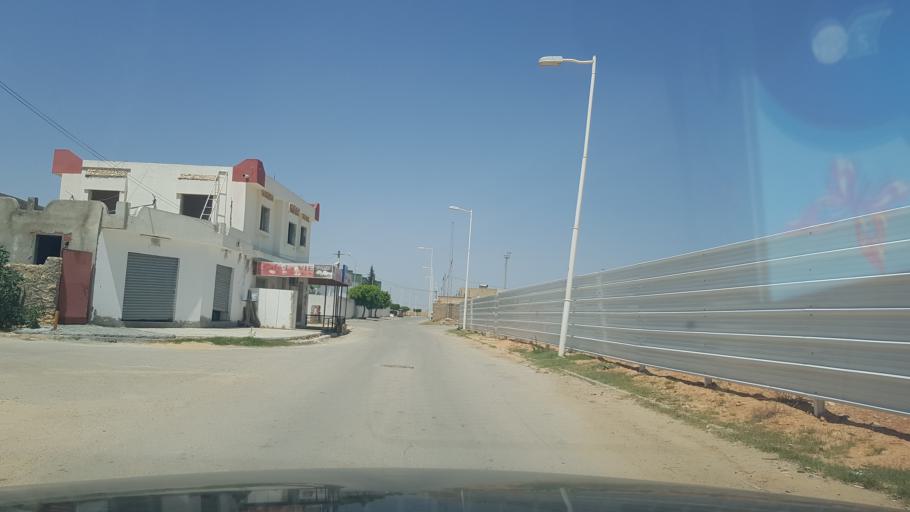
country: TN
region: Safaqis
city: Al Qarmadah
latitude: 34.8408
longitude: 10.7593
